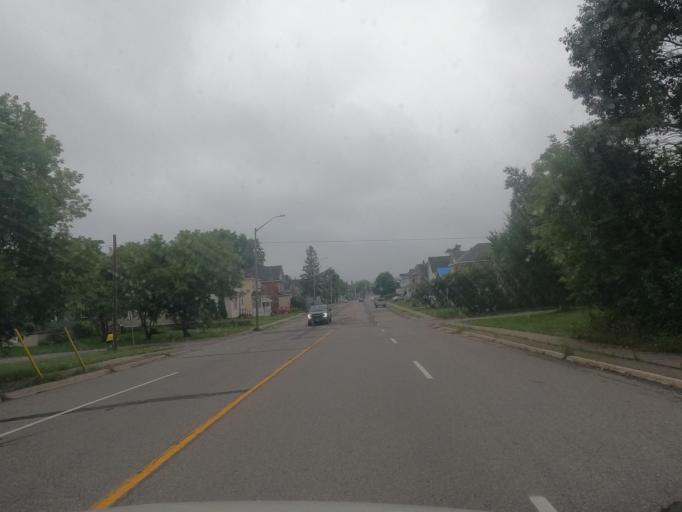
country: CA
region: Ontario
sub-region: Algoma
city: Sault Ste. Marie
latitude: 46.5232
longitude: -84.3467
